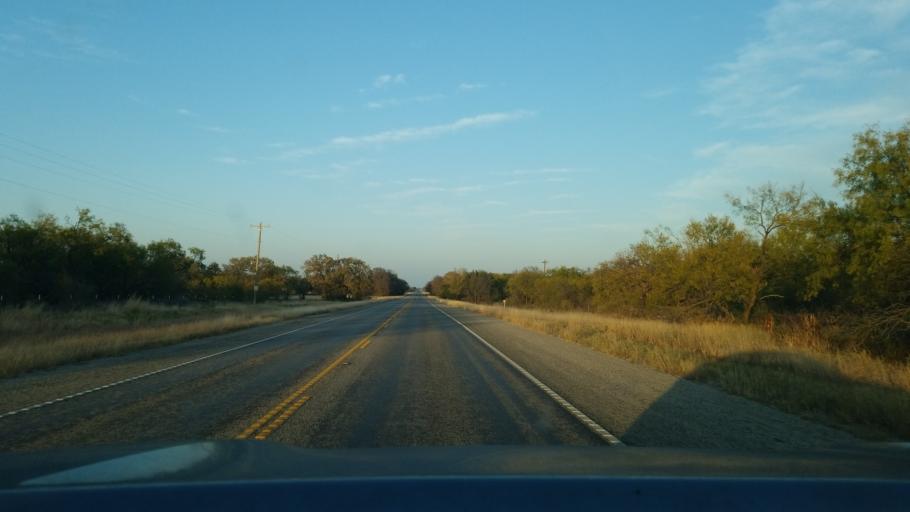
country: US
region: Texas
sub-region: Eastland County
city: Cisco
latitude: 32.4115
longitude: -98.9462
